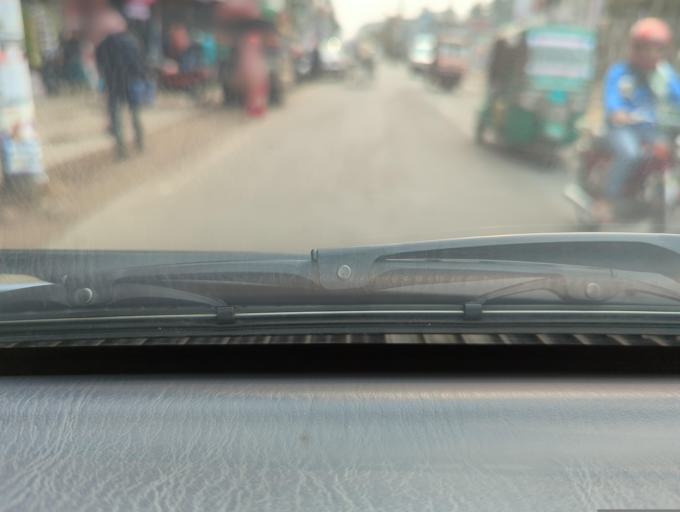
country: BD
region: Sylhet
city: Maulavi Bazar
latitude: 24.4843
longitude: 91.7656
